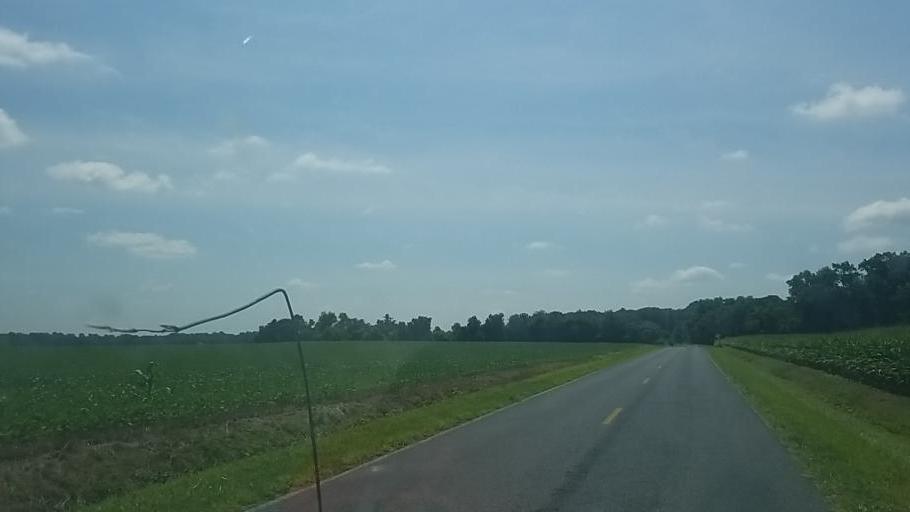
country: US
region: Maryland
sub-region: Caroline County
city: Ridgely
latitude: 38.8968
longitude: -75.9326
